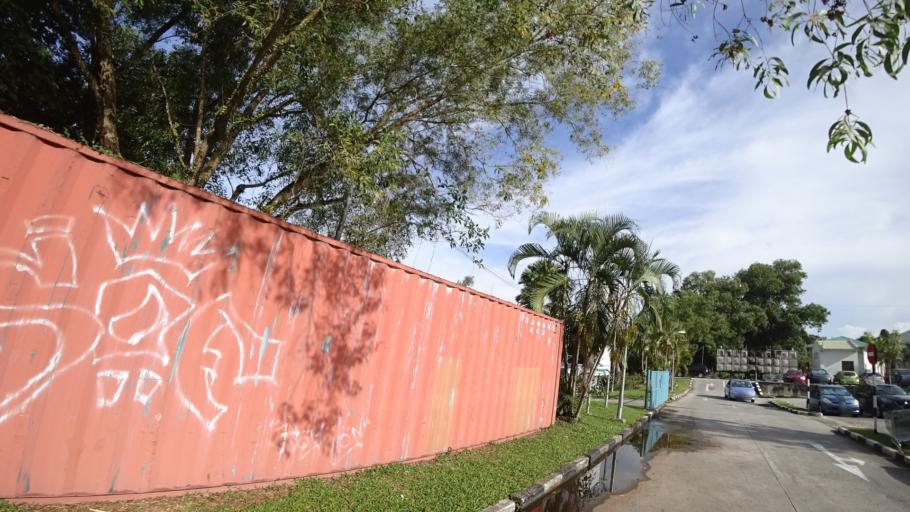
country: BN
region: Brunei and Muara
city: Bandar Seri Begawan
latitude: 4.9007
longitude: 114.9029
